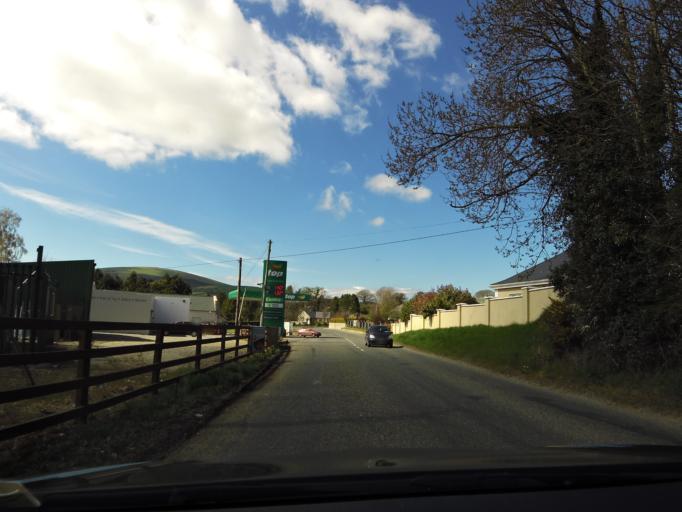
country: IE
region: Leinster
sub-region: Wicklow
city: Carnew
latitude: 52.7938
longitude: -6.4530
